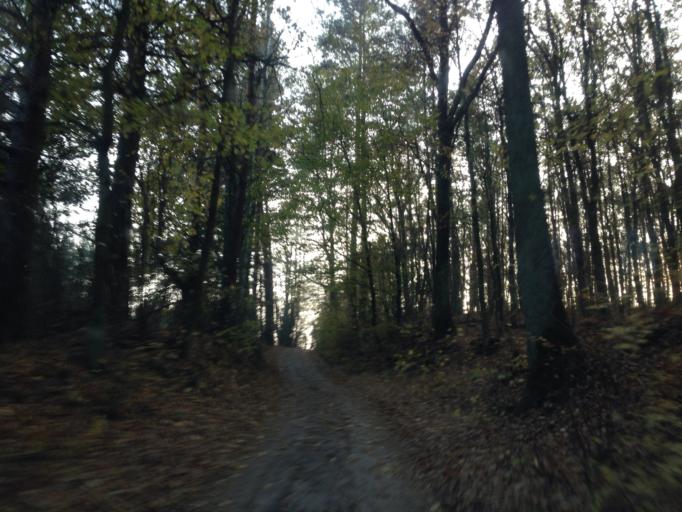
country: PL
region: Kujawsko-Pomorskie
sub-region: Powiat brodnicki
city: Gorzno
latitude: 53.2155
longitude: 19.6516
